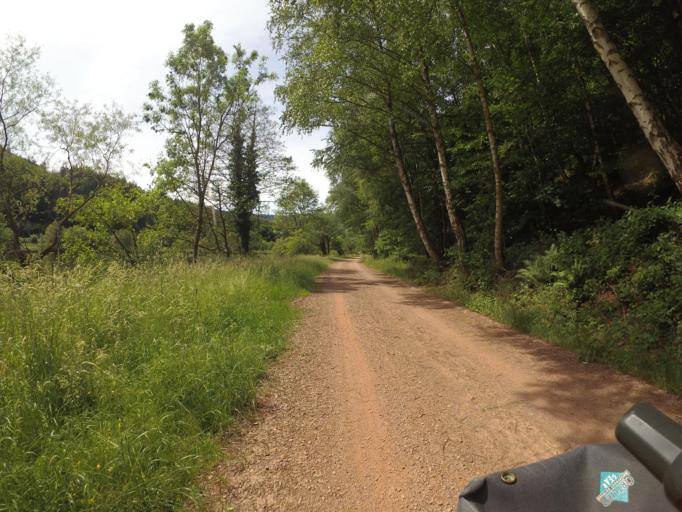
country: DE
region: Rheinland-Pfalz
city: Taben-Rodt
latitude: 49.5463
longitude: 6.6058
